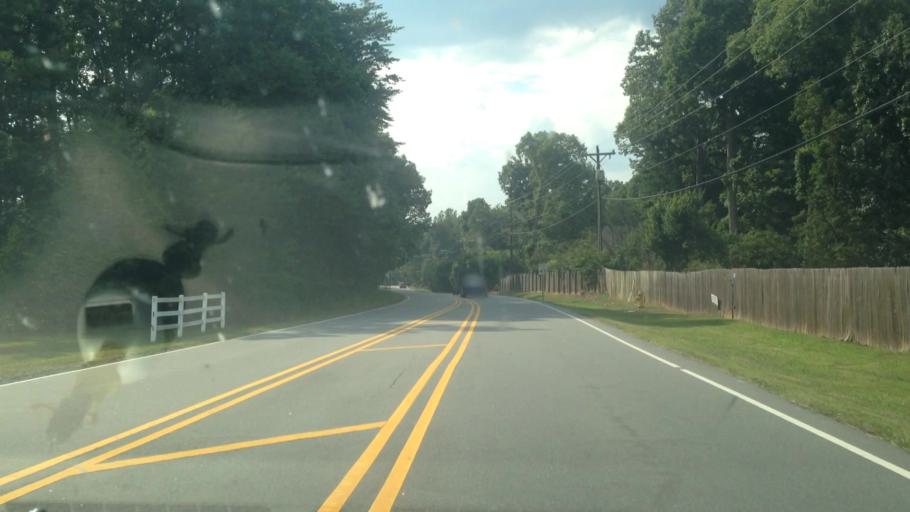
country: US
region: North Carolina
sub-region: Forsyth County
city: Kernersville
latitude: 36.1213
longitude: -80.1073
